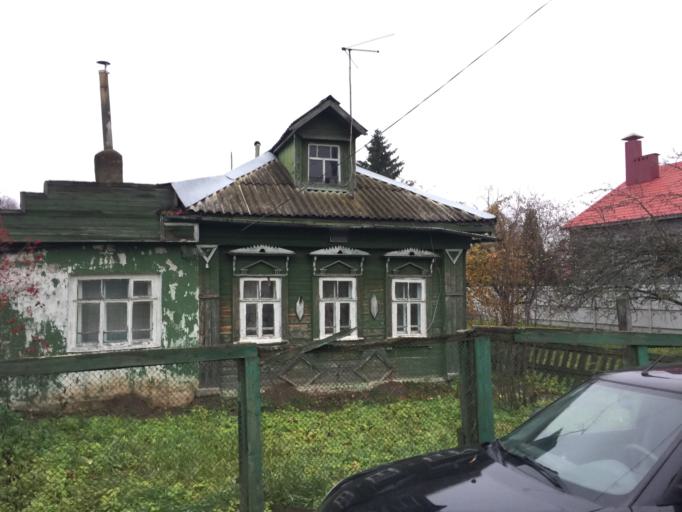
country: RU
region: Jaroslavl
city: Yaroslavl
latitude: 57.7226
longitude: 39.7733
